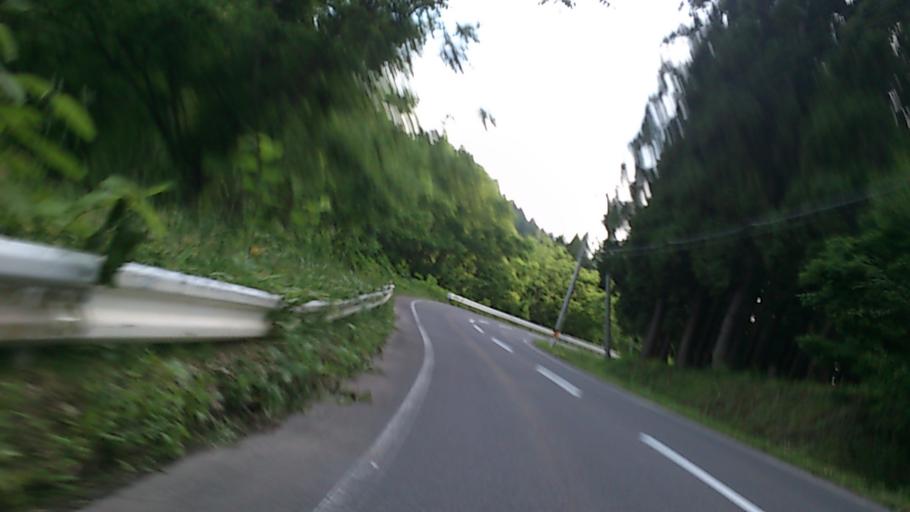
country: JP
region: Aomori
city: Kuroishi
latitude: 40.6426
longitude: 140.7435
